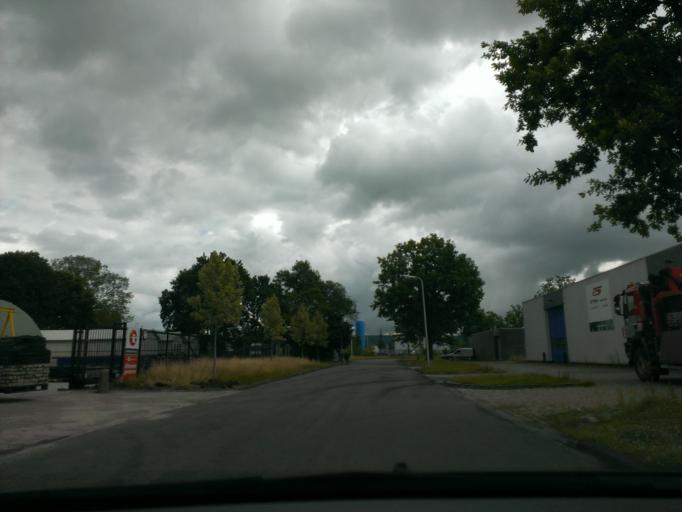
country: NL
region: Drenthe
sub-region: Gemeente Hoogeveen
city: Hoogeveen
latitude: 52.7334
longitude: 6.5024
